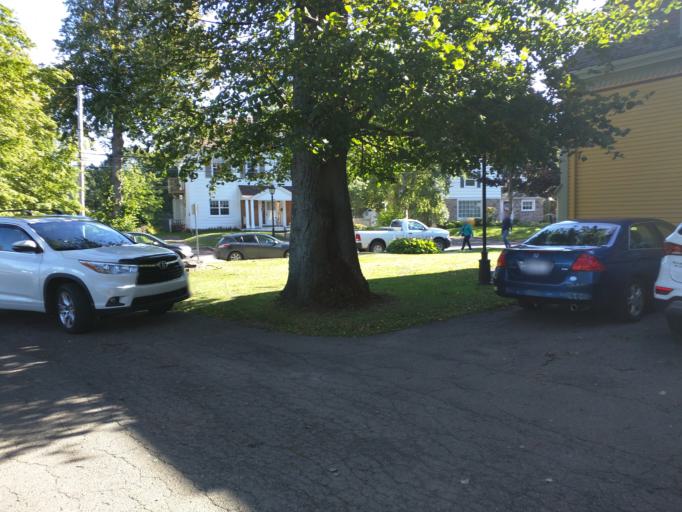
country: CA
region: Prince Edward Island
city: Charlottetown
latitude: 46.2320
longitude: -63.1335
